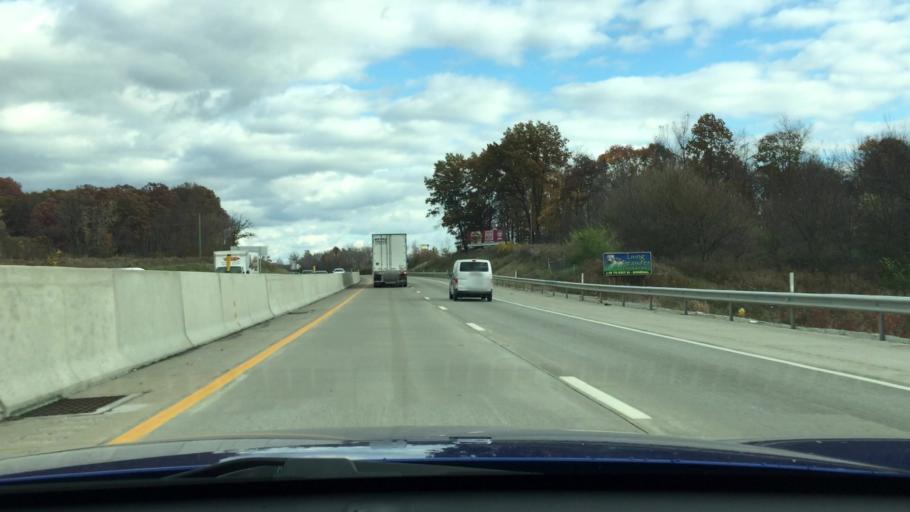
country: US
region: Pennsylvania
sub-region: Westmoreland County
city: New Stanton
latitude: 40.2158
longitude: -79.6278
